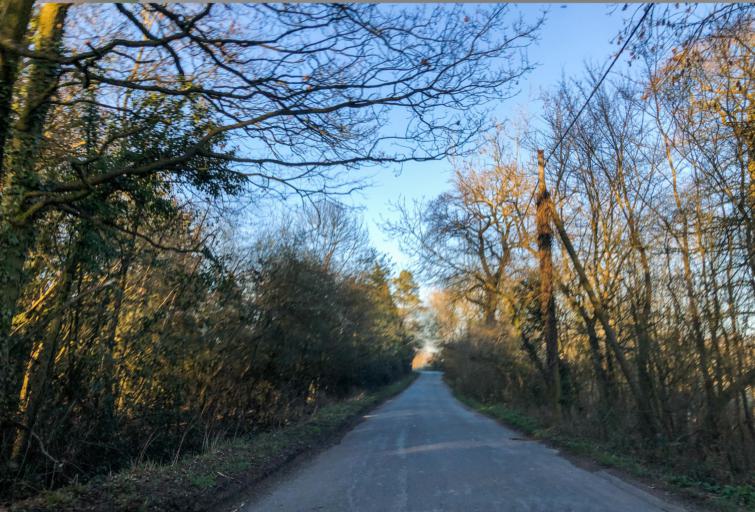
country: GB
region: England
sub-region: Warwickshire
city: Wroxall
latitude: 52.2830
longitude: -1.6662
